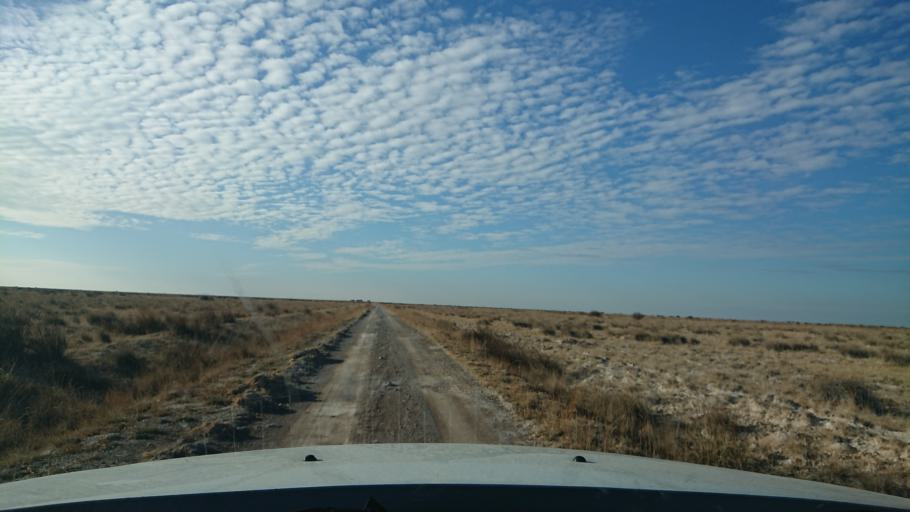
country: TR
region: Aksaray
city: Eskil
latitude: 38.5421
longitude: 33.3332
